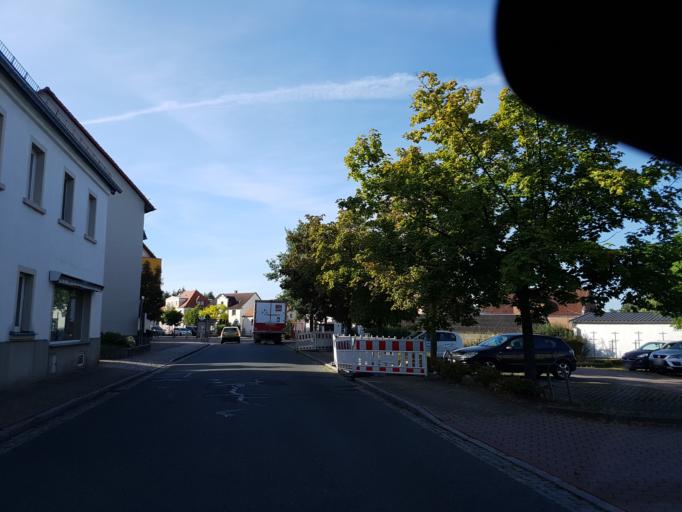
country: DE
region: Saxony
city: Zeithain
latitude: 51.3223
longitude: 13.3182
